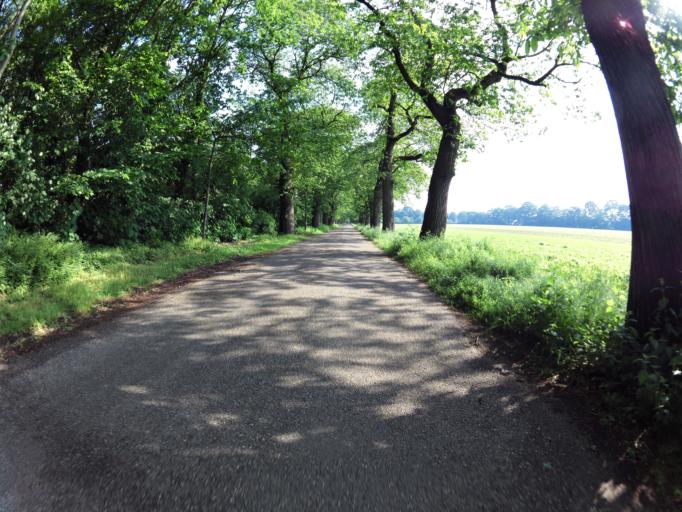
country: NL
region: Limburg
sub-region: Gemeente Roerdalen
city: Montfort
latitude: 51.0847
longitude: 5.9153
